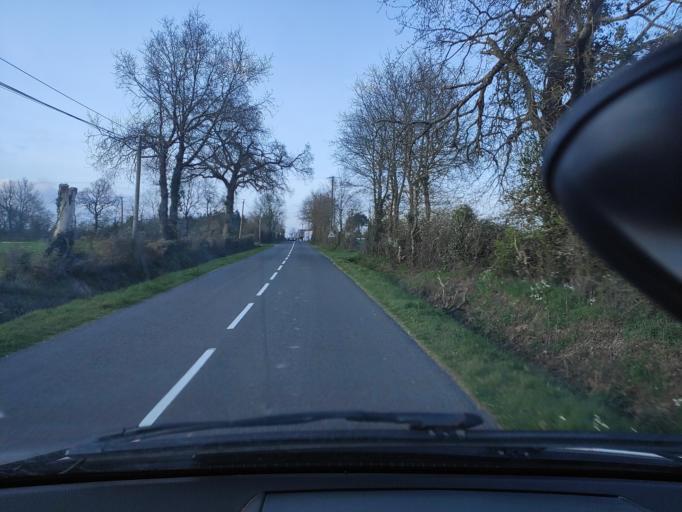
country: FR
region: Pays de la Loire
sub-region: Departement de la Vendee
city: La Chaize-le-Vicomte
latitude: 46.6345
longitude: -1.3028
